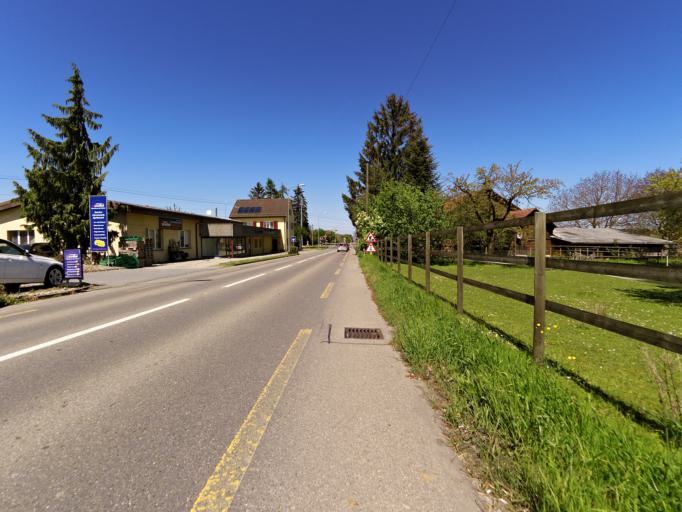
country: CH
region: Thurgau
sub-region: Weinfelden District
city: Berg
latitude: 47.6116
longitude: 9.1697
